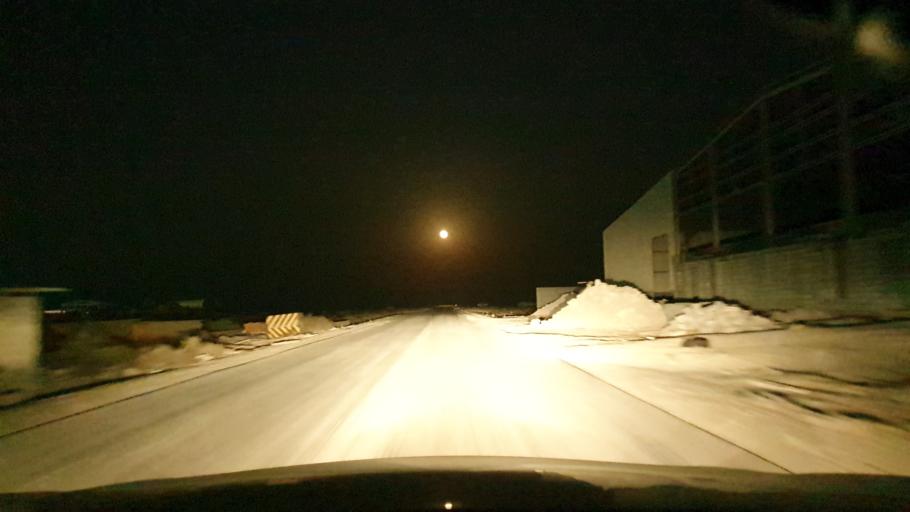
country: BH
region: Northern
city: Sitrah
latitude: 26.0973
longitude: 50.6258
